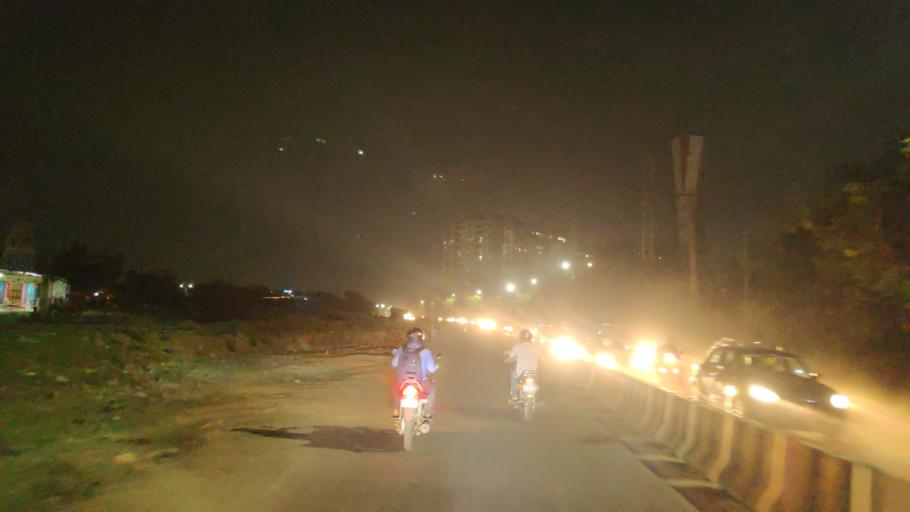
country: IN
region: Telangana
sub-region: Rangareddi
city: Kukatpalli
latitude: 17.4734
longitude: 78.3843
